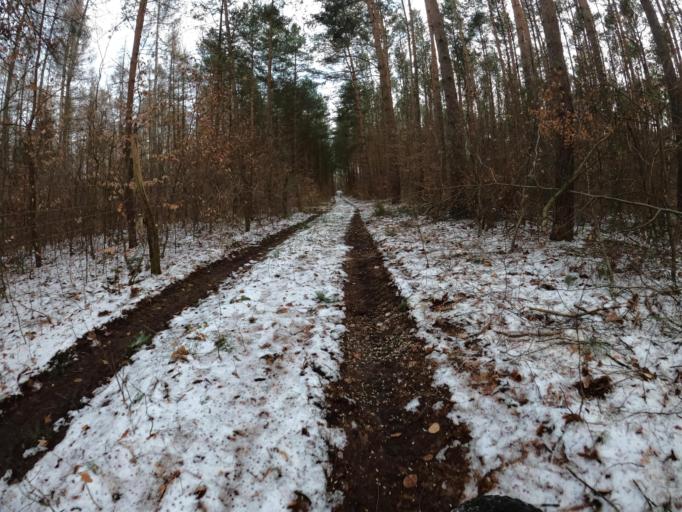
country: PL
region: Lubusz
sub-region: Powiat slubicki
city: Cybinka
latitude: 52.1932
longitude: 14.8692
